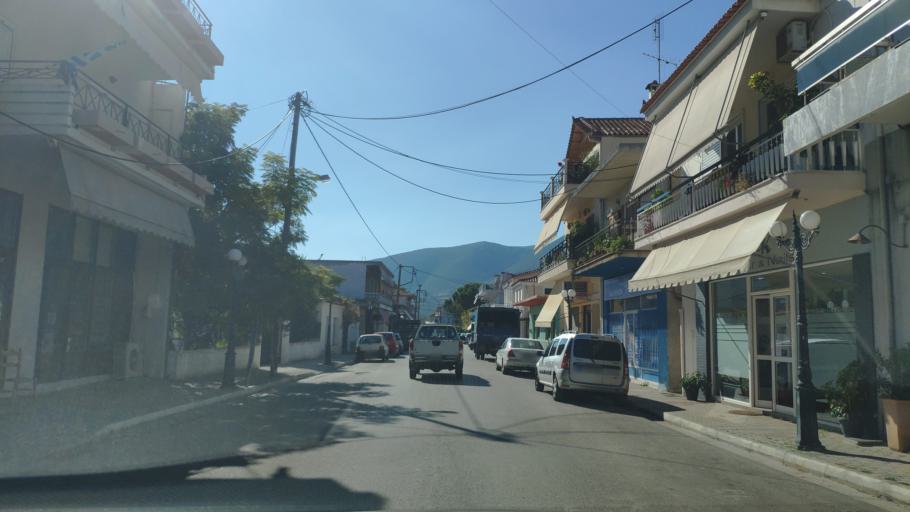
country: GR
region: Peloponnese
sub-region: Nomos Korinthias
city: Khiliomodhi
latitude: 37.8096
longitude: 22.8698
